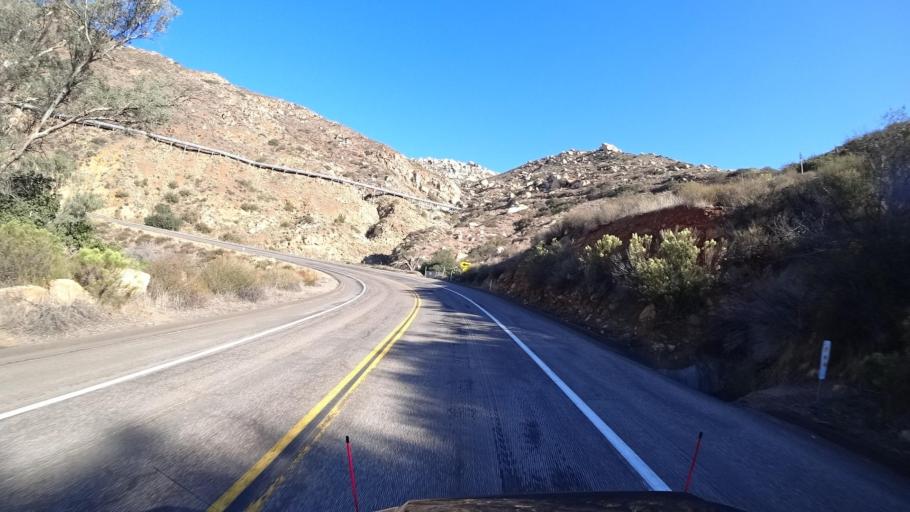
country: MX
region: Baja California
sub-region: Tecate
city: Lomas de Santa Anita
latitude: 32.6181
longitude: -116.7274
